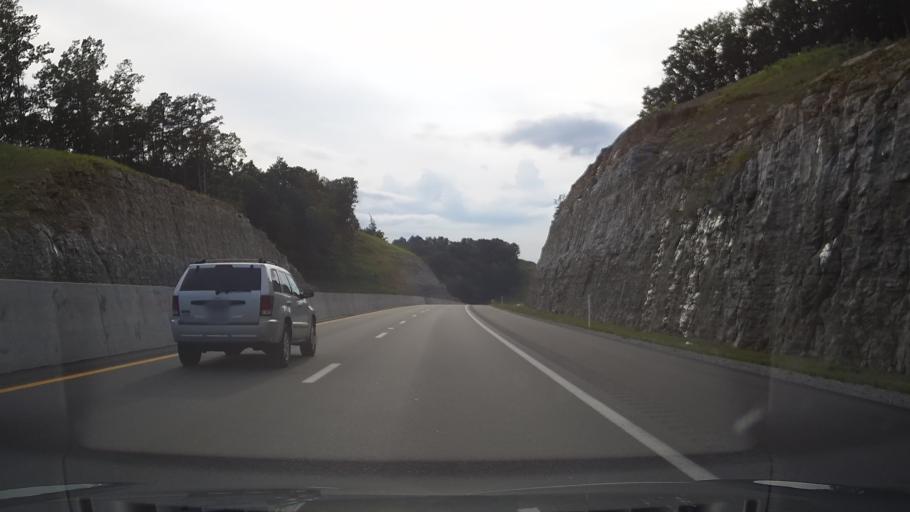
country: US
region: Ohio
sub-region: Scioto County
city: Lucasville
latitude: 38.8688
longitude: -82.9298
